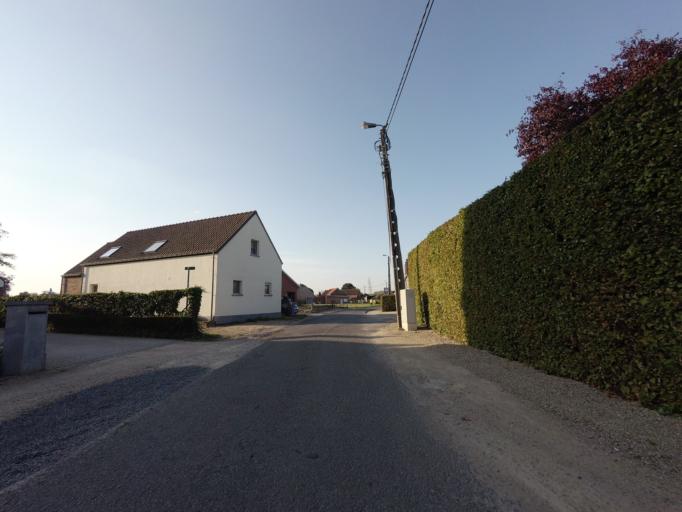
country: BE
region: Flanders
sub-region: Provincie Vlaams-Brabant
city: Haacht
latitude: 50.9443
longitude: 4.6154
